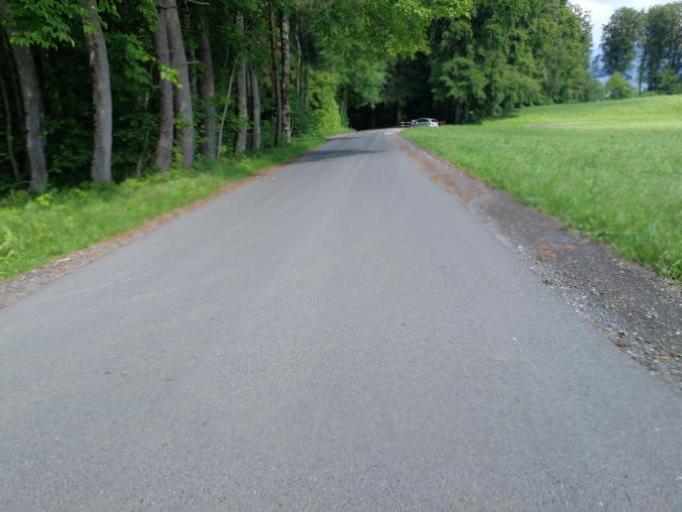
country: CH
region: Schwyz
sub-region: Bezirk Hoefe
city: Freienbach
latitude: 47.1864
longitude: 8.7741
